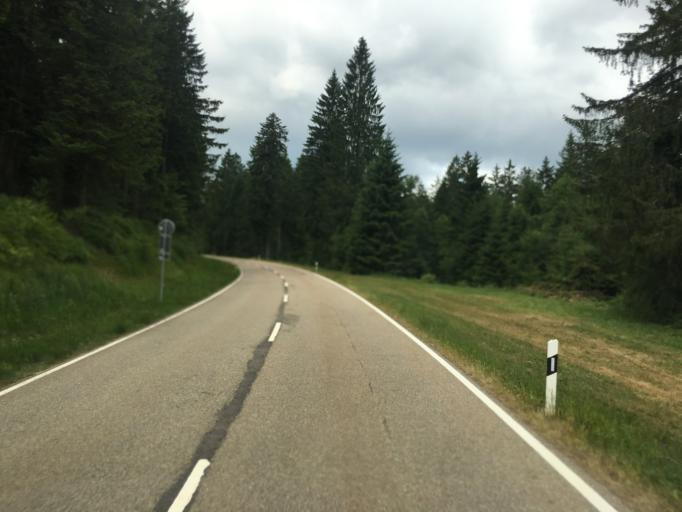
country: DE
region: Baden-Wuerttemberg
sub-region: Karlsruhe Region
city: Biberach
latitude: 48.6604
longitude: 8.2560
